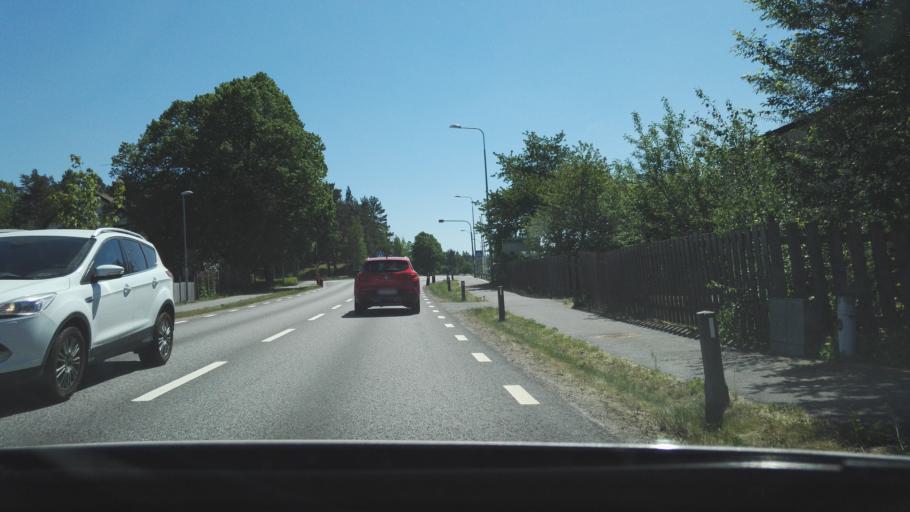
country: SE
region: Kronoberg
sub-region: Vaxjo Kommun
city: Ingelstad
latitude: 56.6400
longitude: 14.9209
